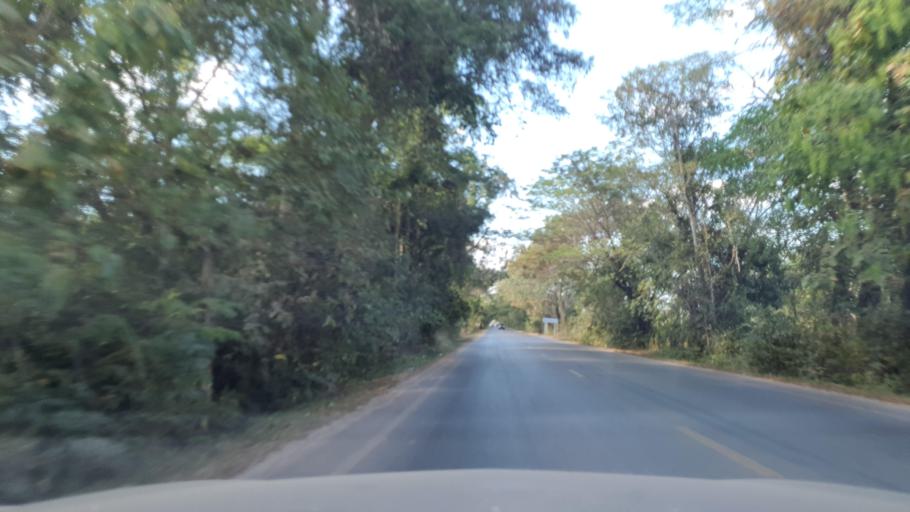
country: TH
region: Nakhon Phanom
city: Ban Phaeng
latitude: 18.0204
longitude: 104.1506
